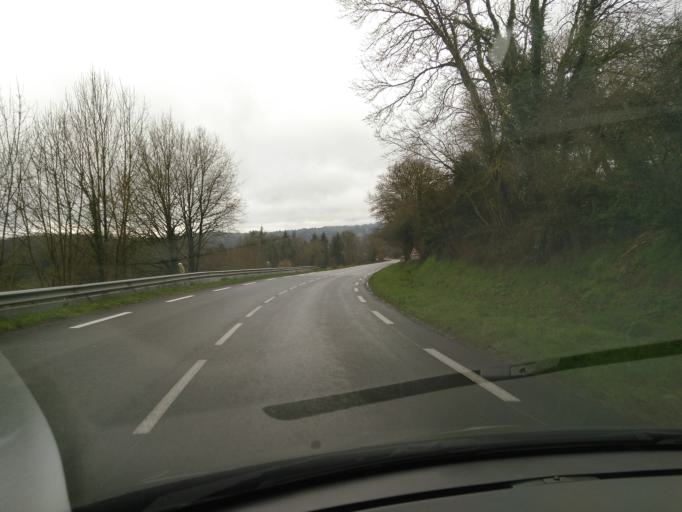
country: FR
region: Limousin
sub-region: Departement de la Haute-Vienne
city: Le Vigen
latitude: 45.7646
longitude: 1.2963
